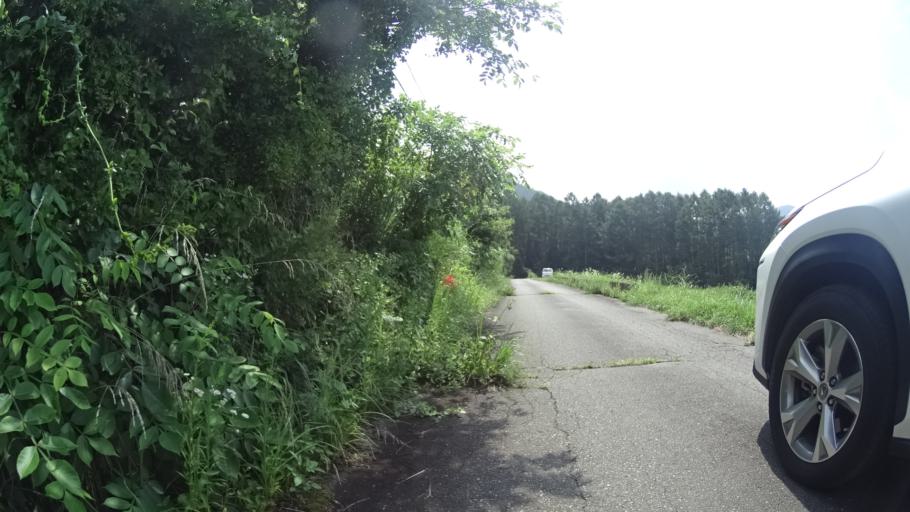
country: JP
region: Yamanashi
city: Nirasaki
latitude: 35.8893
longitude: 138.4746
